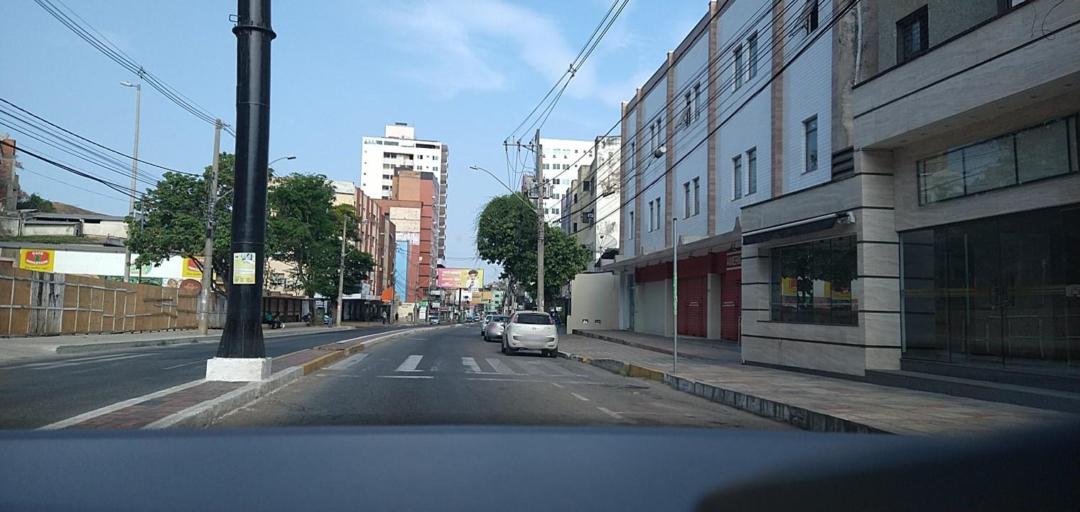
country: BR
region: Minas Gerais
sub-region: Joao Monlevade
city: Joao Monlevade
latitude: -19.8076
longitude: -43.1748
